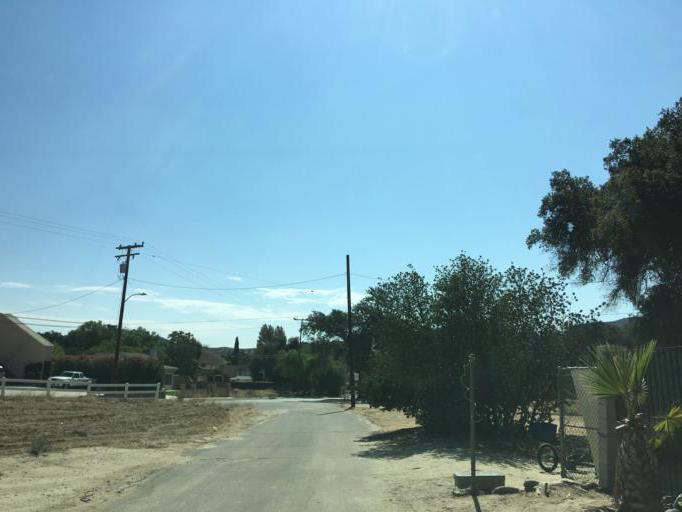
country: US
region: California
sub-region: Los Angeles County
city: Val Verde
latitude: 34.4459
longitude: -118.6618
